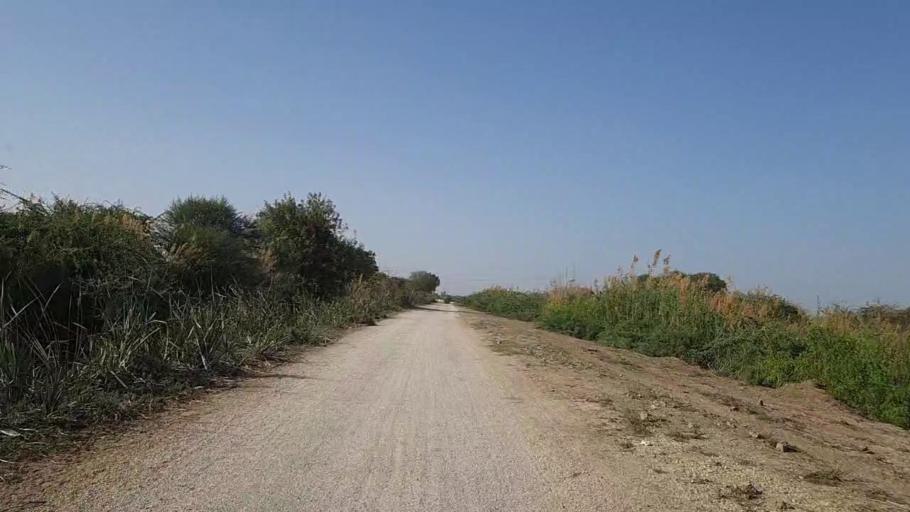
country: PK
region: Sindh
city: Kotri
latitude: 25.1459
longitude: 68.2655
